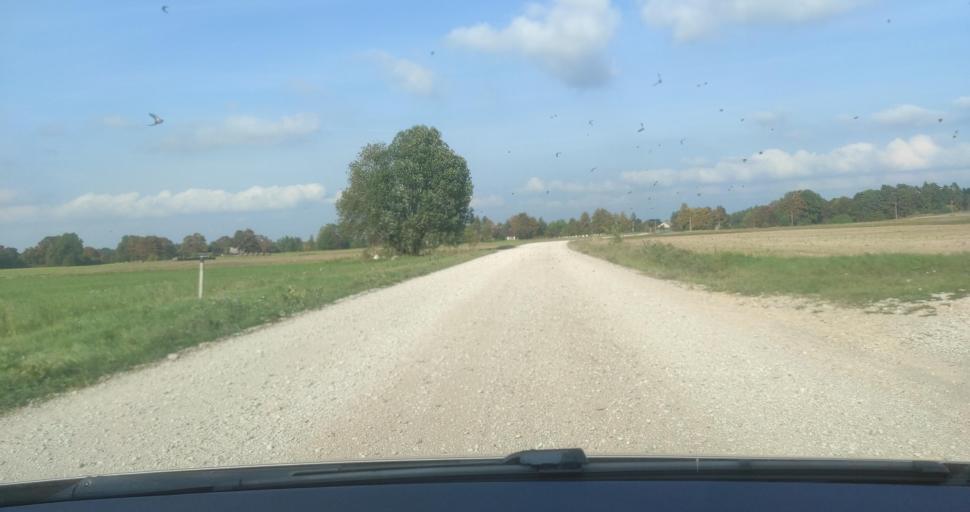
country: LV
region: Alsunga
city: Alsunga
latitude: 56.9932
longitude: 21.5813
